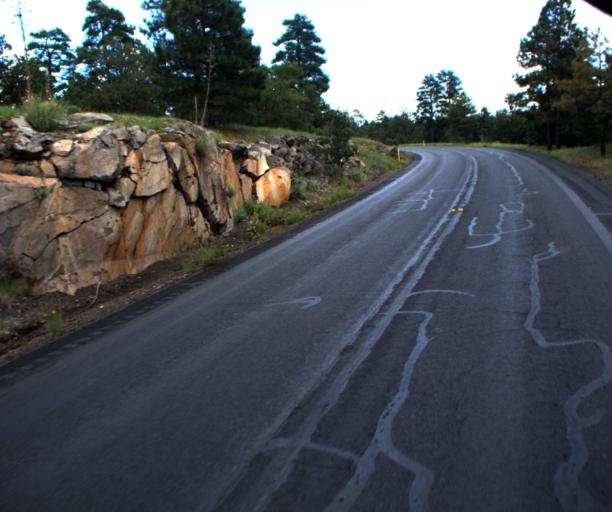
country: US
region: Arizona
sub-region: Gila County
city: Pine
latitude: 34.5141
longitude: -111.4883
